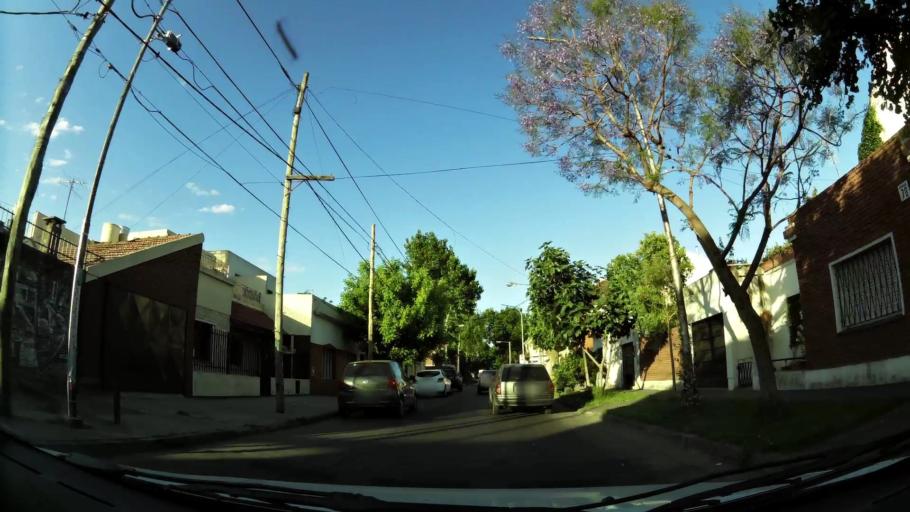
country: AR
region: Buenos Aires
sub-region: Partido de General San Martin
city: General San Martin
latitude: -34.5697
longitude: -58.5466
